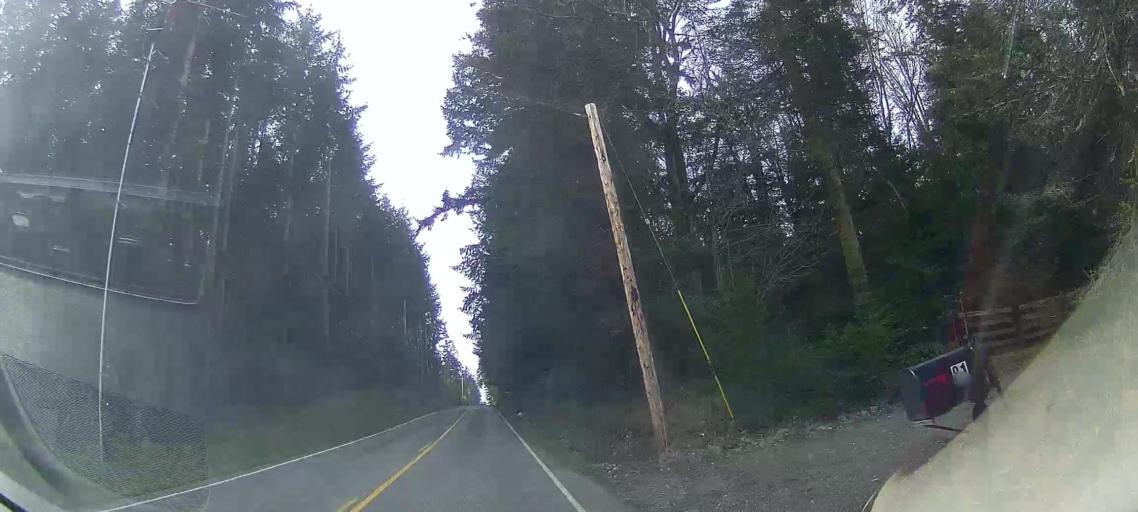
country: US
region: Washington
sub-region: Island County
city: Camano
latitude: 48.1383
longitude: -122.4803
